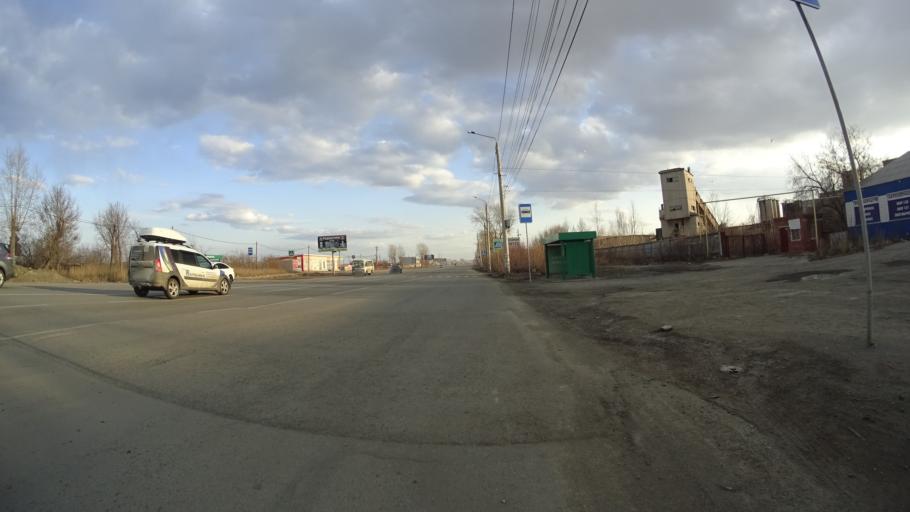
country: RU
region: Chelyabinsk
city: Novosineglazovskiy
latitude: 55.0981
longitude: 61.3876
